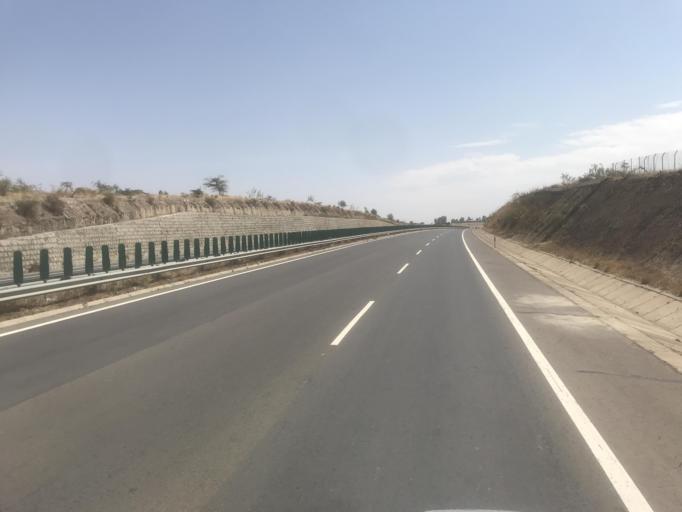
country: ET
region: Oromiya
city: Mojo
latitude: 8.5839
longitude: 39.1669
